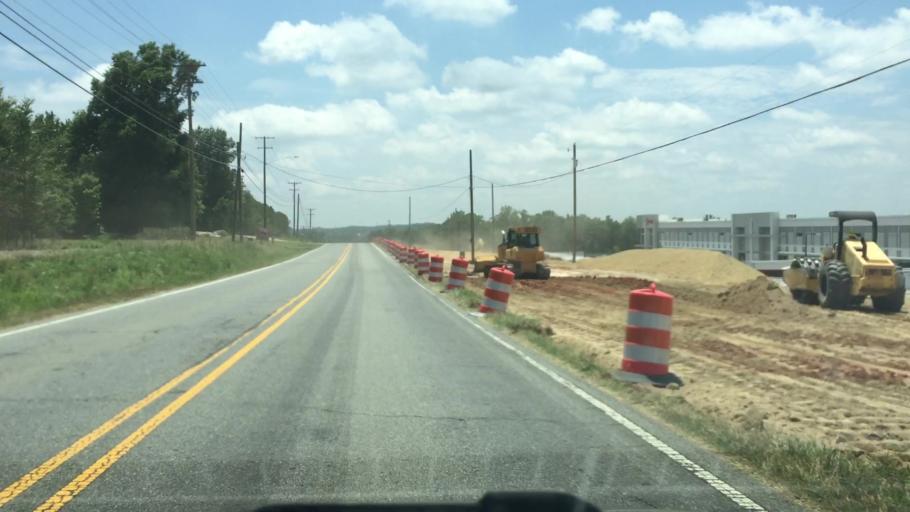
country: US
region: North Carolina
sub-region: Cabarrus County
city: Harrisburg
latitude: 35.3974
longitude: -80.7167
